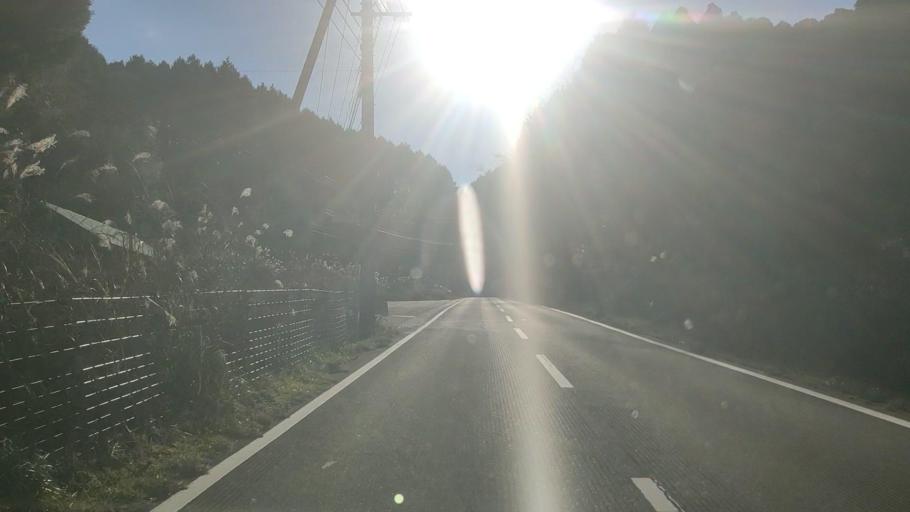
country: JP
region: Saga Prefecture
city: Kanzakimachi-kanzaki
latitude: 33.4139
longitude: 130.2765
